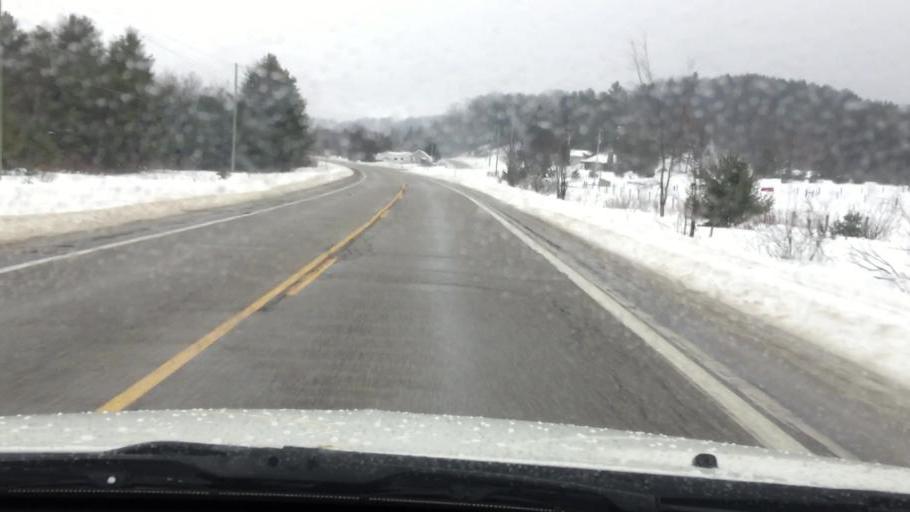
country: US
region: Michigan
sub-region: Charlevoix County
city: East Jordan
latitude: 45.1144
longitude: -85.1294
